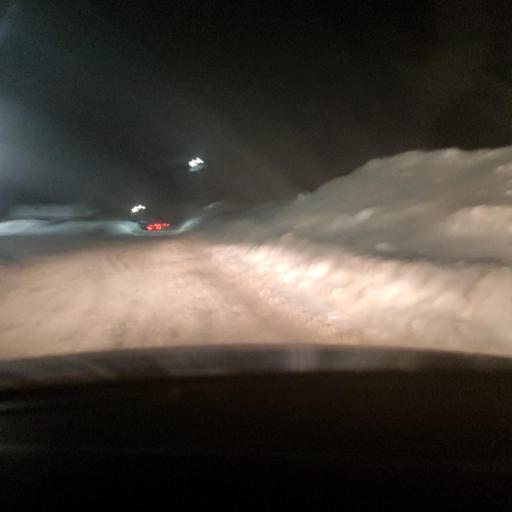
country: RU
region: Tatarstan
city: Stolbishchi
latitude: 55.7185
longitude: 49.3552
